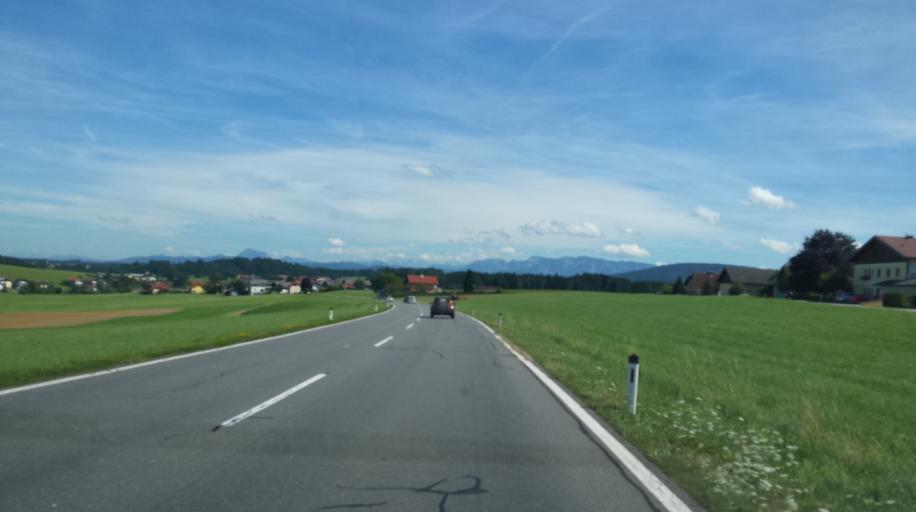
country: AT
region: Upper Austria
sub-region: Politischer Bezirk Vocklabruck
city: Frankenmarkt
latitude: 47.9915
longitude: 13.3568
